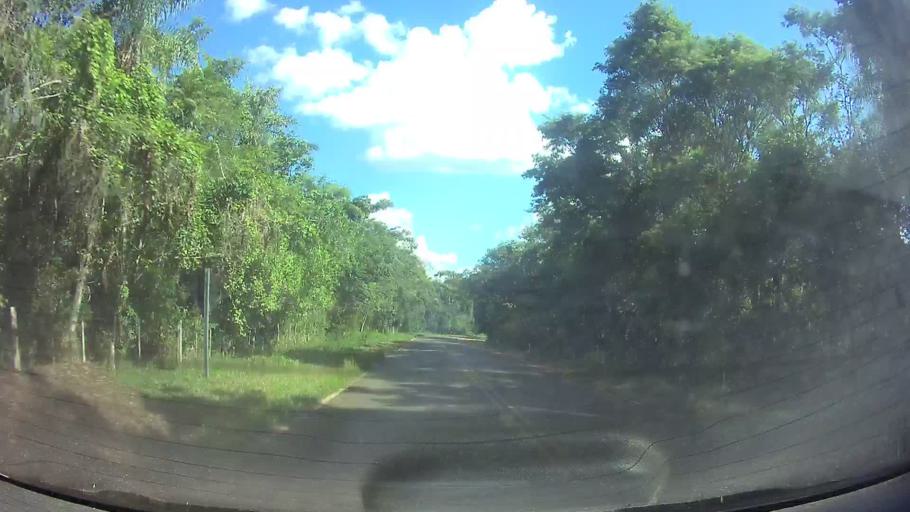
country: PY
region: Paraguari
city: Sapucai
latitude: -25.6658
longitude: -56.8577
